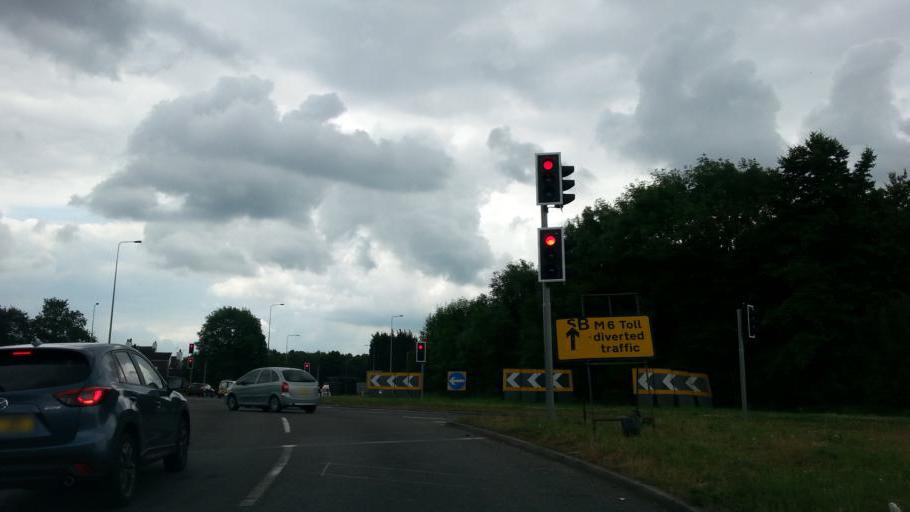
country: GB
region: England
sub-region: City and Borough of Birmingham
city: Sutton Coldfield
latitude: 52.5915
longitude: -1.7838
